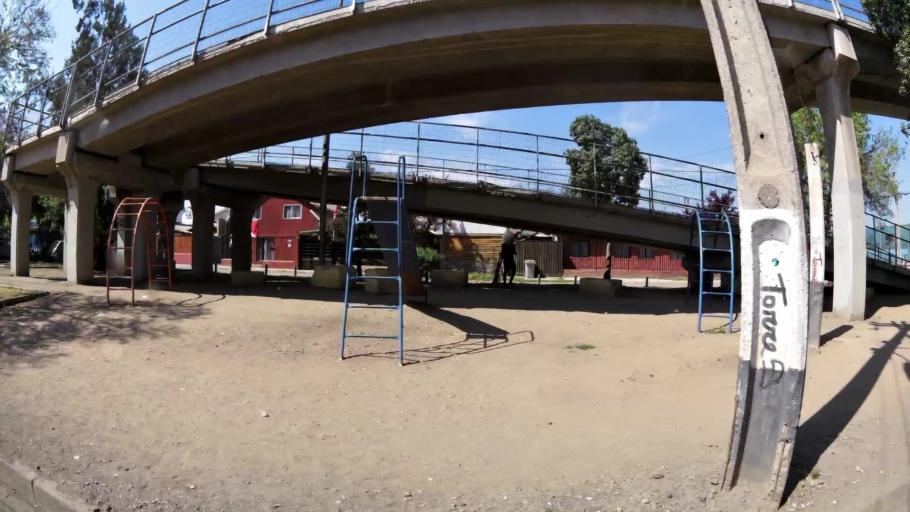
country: CL
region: Santiago Metropolitan
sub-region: Provincia de Santiago
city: Lo Prado
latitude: -33.3974
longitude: -70.6990
